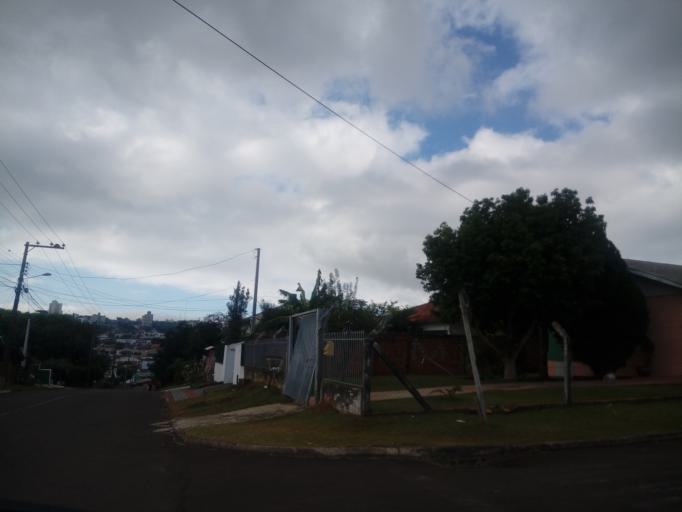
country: BR
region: Santa Catarina
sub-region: Chapeco
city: Chapeco
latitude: -27.1159
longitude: -52.6228
